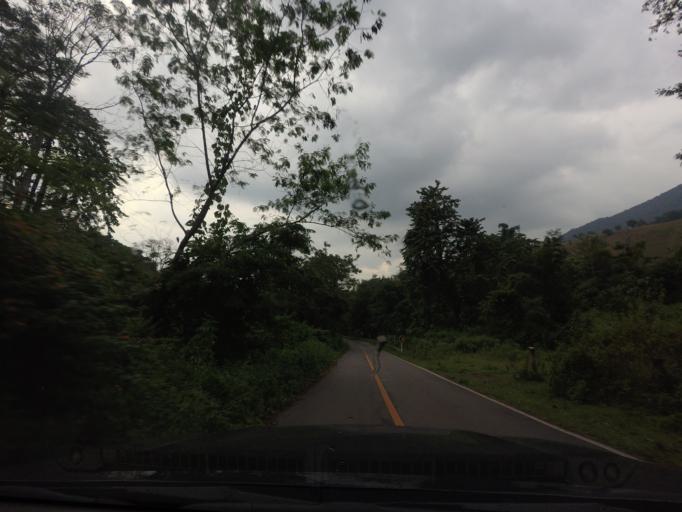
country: TH
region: Nan
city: Bo Kluea
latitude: 19.3256
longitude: 101.1717
